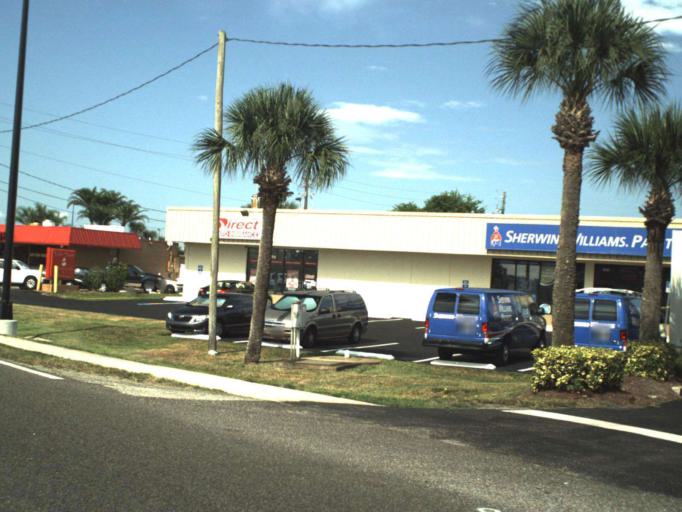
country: US
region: Florida
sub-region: Seminole County
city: Lake Mary
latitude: 28.7590
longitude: -81.2859
